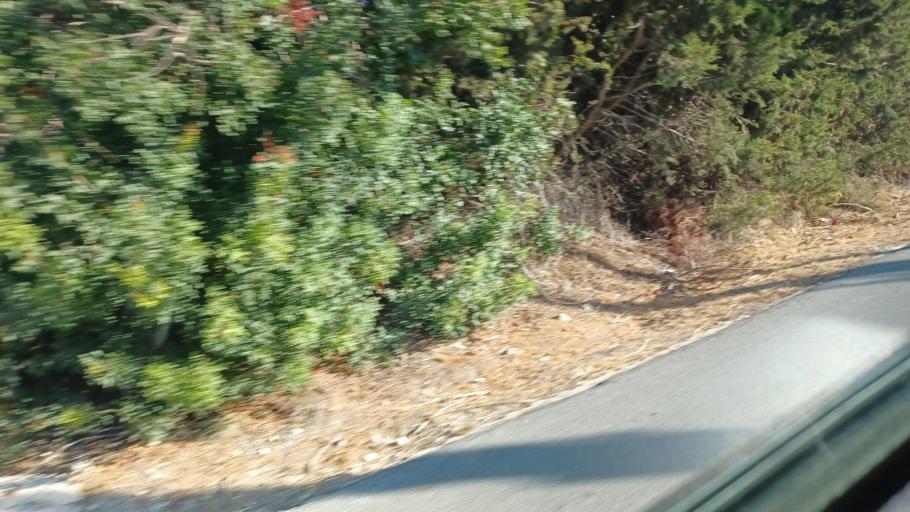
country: CY
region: Pafos
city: Tala
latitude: 34.8452
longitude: 32.4402
